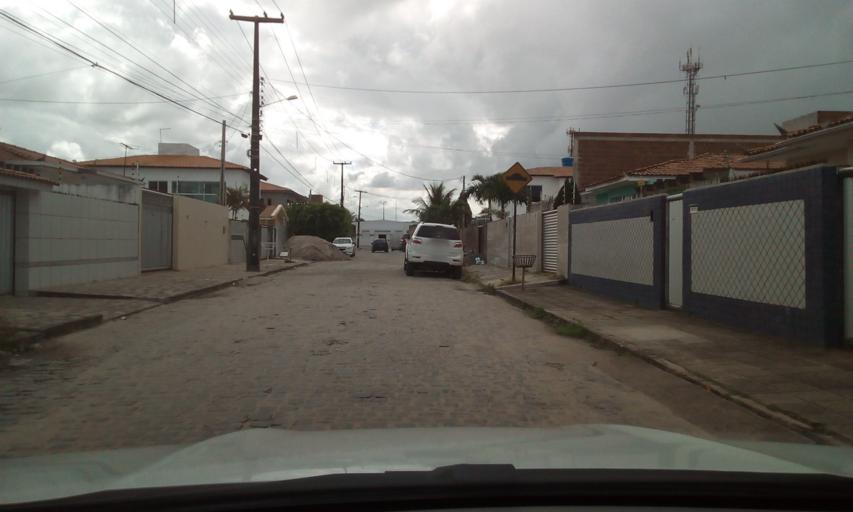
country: BR
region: Paraiba
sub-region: Joao Pessoa
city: Joao Pessoa
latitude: -7.1798
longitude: -34.8754
